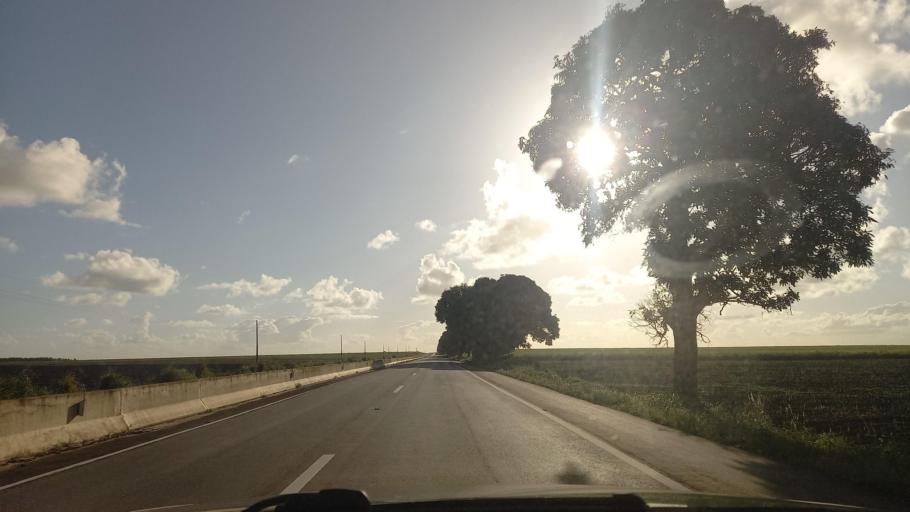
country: BR
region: Alagoas
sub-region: Sao Miguel Dos Campos
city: Sao Miguel dos Campos
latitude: -9.8022
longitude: -36.1481
